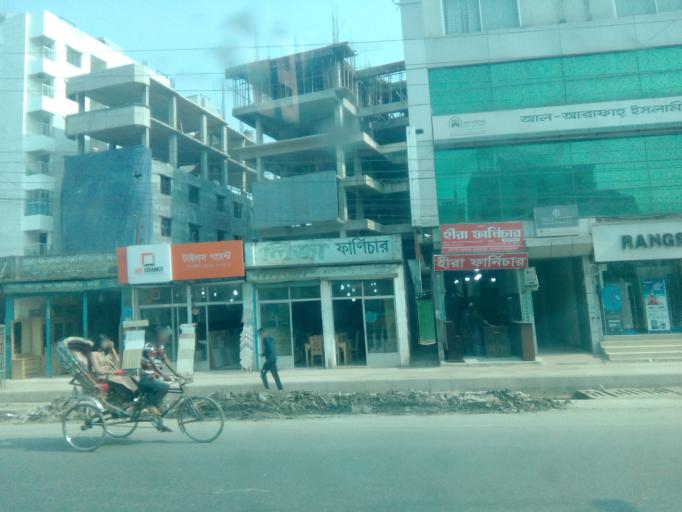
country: BD
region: Dhaka
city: Paltan
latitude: 23.7823
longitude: 90.4258
